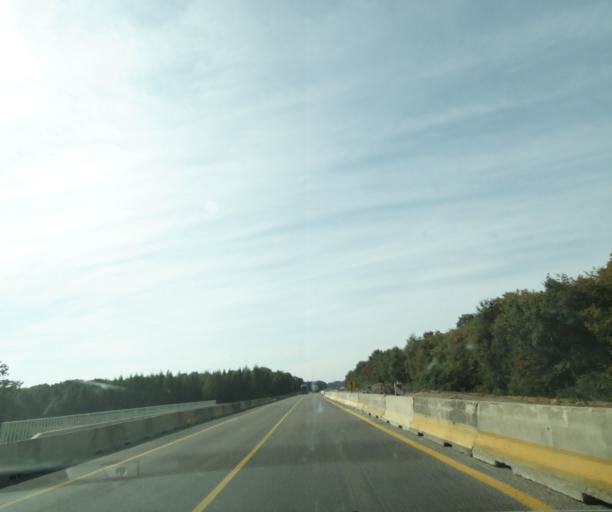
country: FR
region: Bourgogne
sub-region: Departement de Saone-et-Loire
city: Paray-le-Monial
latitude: 46.4951
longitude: 4.1574
